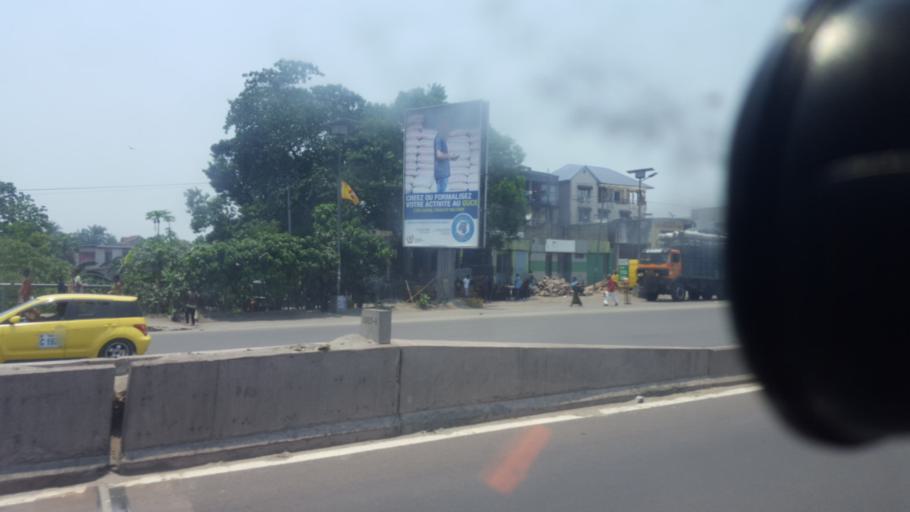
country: CD
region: Kinshasa
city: Masina
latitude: -4.3877
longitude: 15.3666
